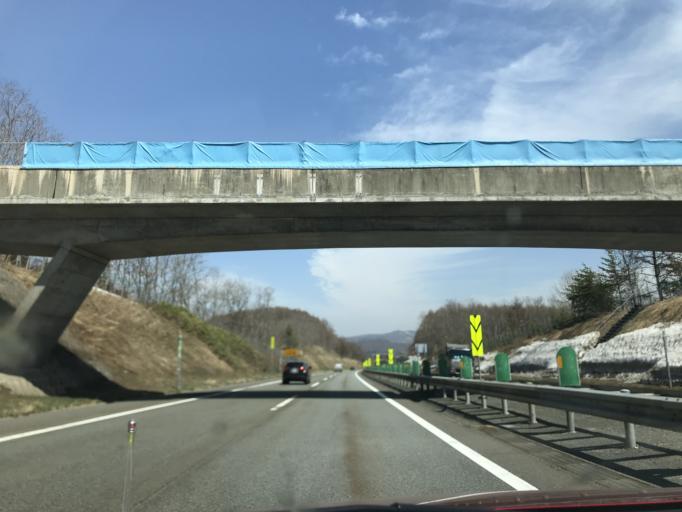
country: JP
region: Hokkaido
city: Iwamizawa
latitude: 43.2110
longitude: 141.8186
